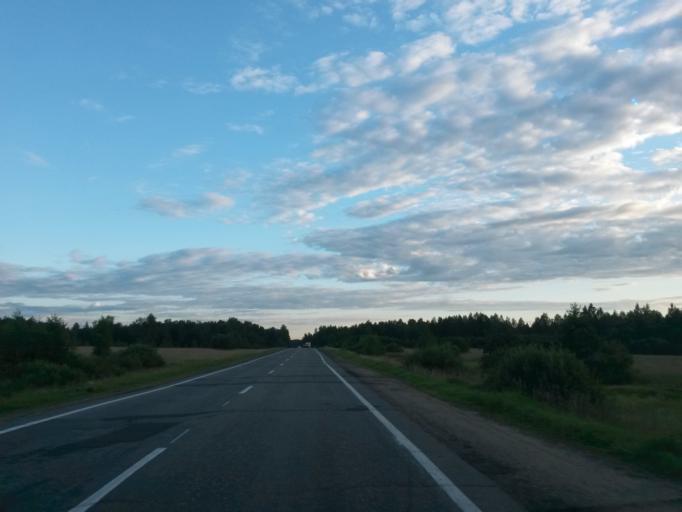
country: RU
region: Jaroslavl
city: Gavrilov-Yam
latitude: 57.3951
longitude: 39.9182
